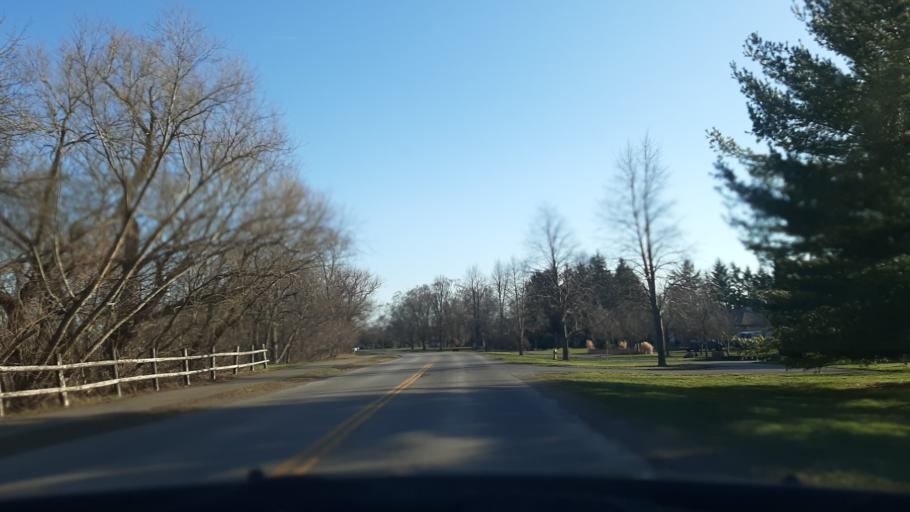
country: US
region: New York
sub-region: Niagara County
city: Youngstown
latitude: 43.2167
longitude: -79.0602
